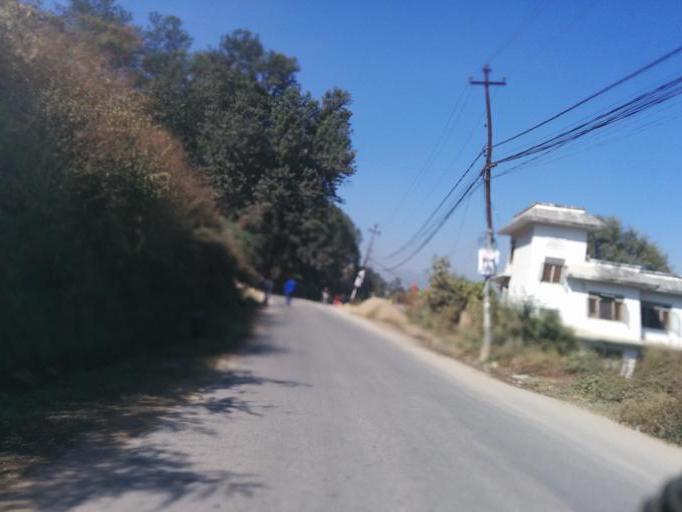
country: NP
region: Central Region
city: Kirtipur
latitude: 27.6802
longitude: 85.2769
